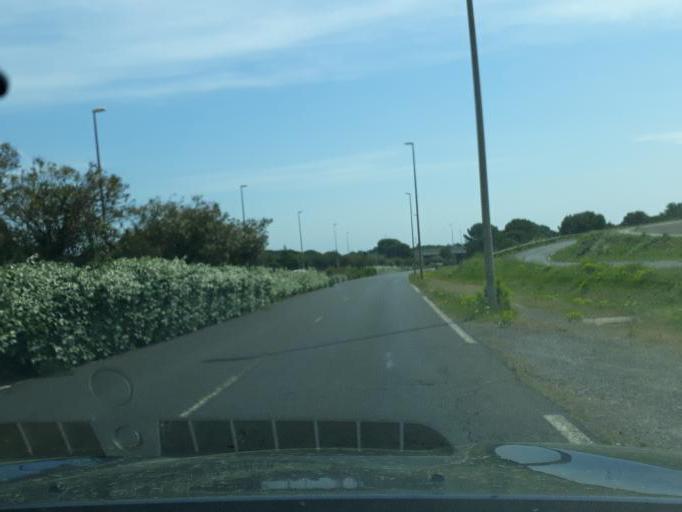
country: FR
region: Languedoc-Roussillon
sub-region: Departement de l'Herault
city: Le Cap d'Agde
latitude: 43.2949
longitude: 3.4998
